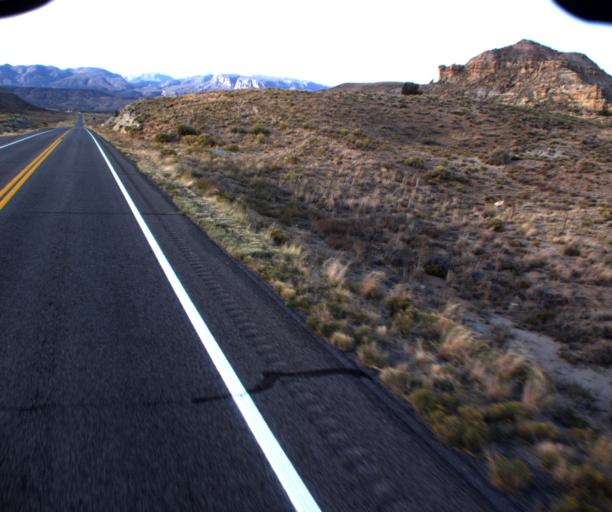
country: US
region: New Mexico
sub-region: San Juan County
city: Shiprock
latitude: 36.9460
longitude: -109.0732
